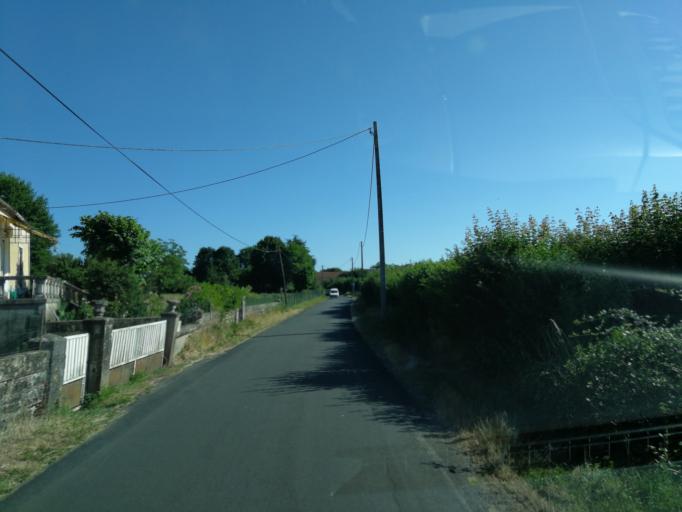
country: FR
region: Midi-Pyrenees
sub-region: Departement du Lot
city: Gourdon
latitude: 44.8268
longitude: 1.3605
